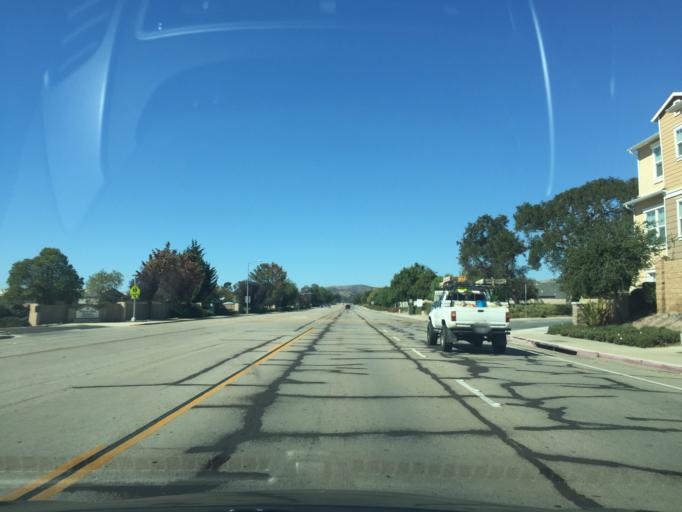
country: US
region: California
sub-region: Santa Barbara County
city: Buellton
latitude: 34.6157
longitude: -120.1993
